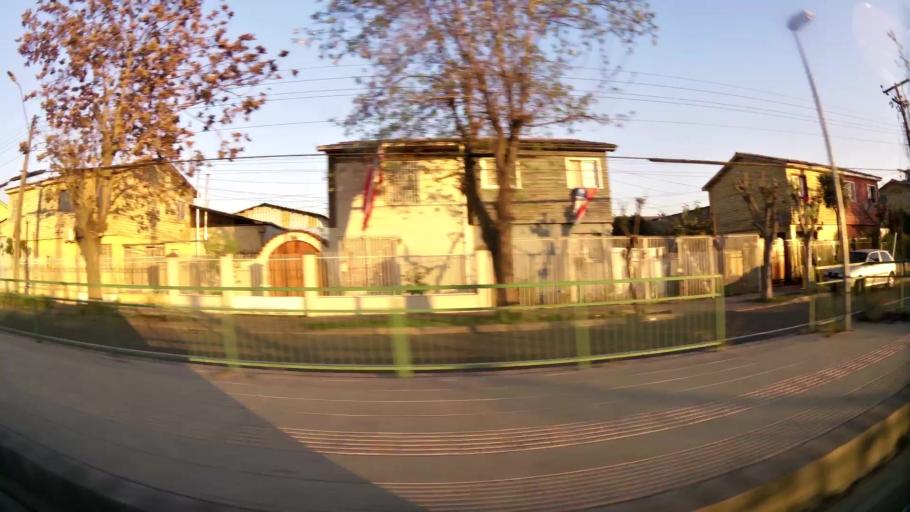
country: CL
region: Santiago Metropolitan
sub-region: Provincia de Santiago
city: Santiago
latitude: -33.4717
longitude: -70.6823
